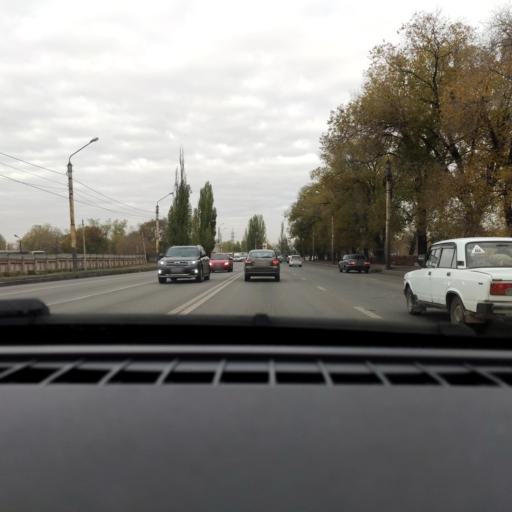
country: RU
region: Voronezj
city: Voronezh
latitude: 51.6269
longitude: 39.2312
